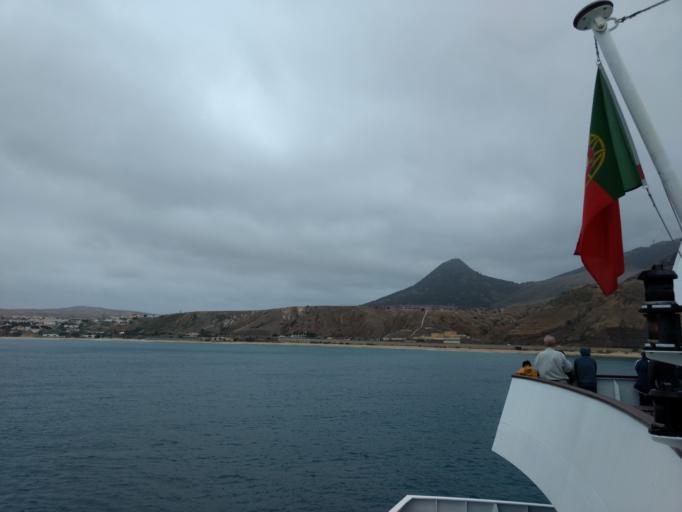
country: PT
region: Madeira
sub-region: Porto Santo
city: Vila de Porto Santo
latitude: 33.0580
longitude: -16.3181
